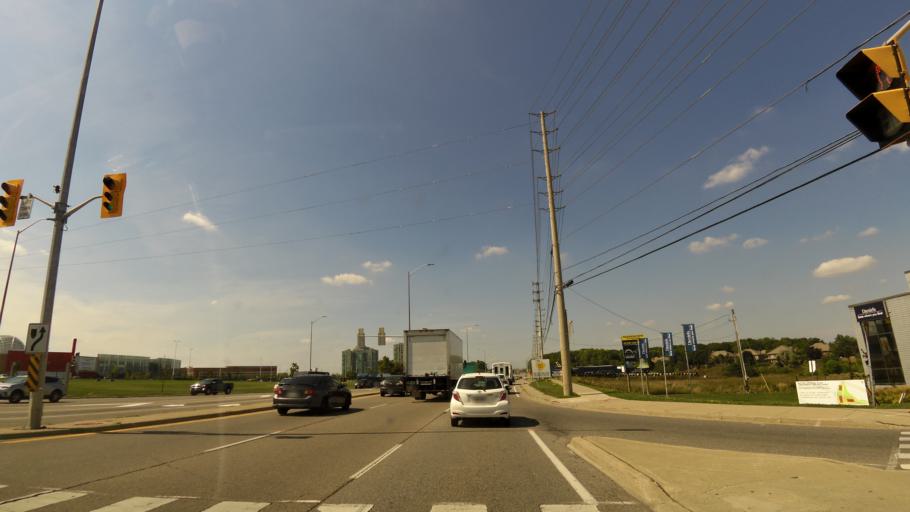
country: CA
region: Ontario
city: Mississauga
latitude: 43.5590
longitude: -79.7067
